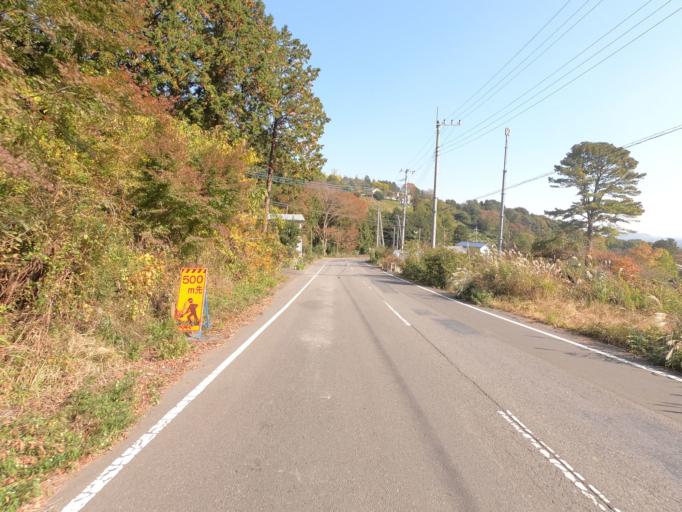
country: JP
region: Ibaraki
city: Tsukuba
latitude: 36.2312
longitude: 140.1378
